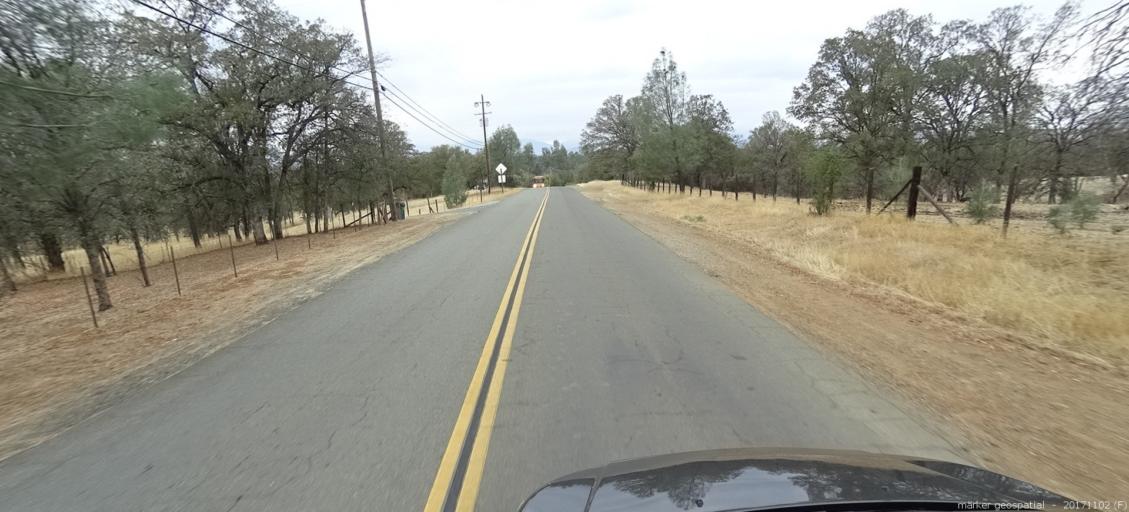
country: US
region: California
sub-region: Shasta County
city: Shasta Lake
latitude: 40.6521
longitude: -122.3119
